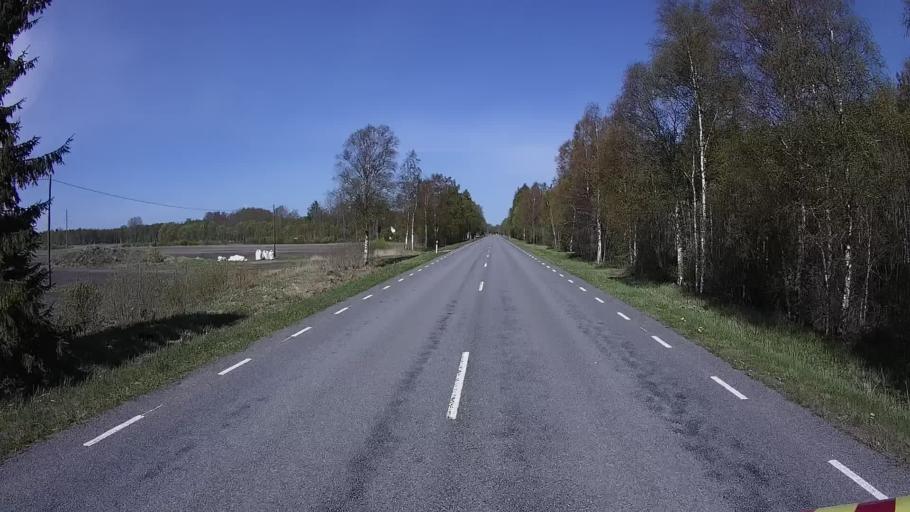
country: EE
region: Laeaene
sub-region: Lihula vald
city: Lihula
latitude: 58.6415
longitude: 23.8546
